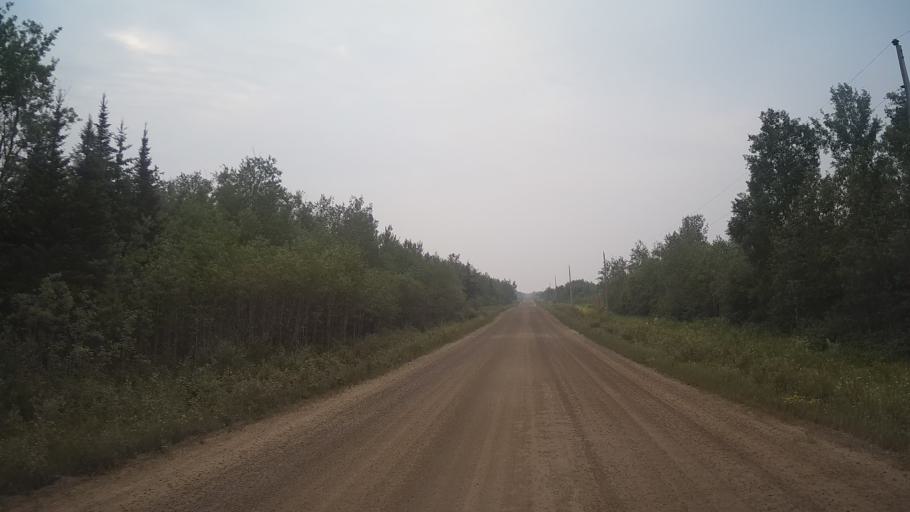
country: CA
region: Ontario
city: Hearst
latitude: 49.6388
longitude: -83.2783
